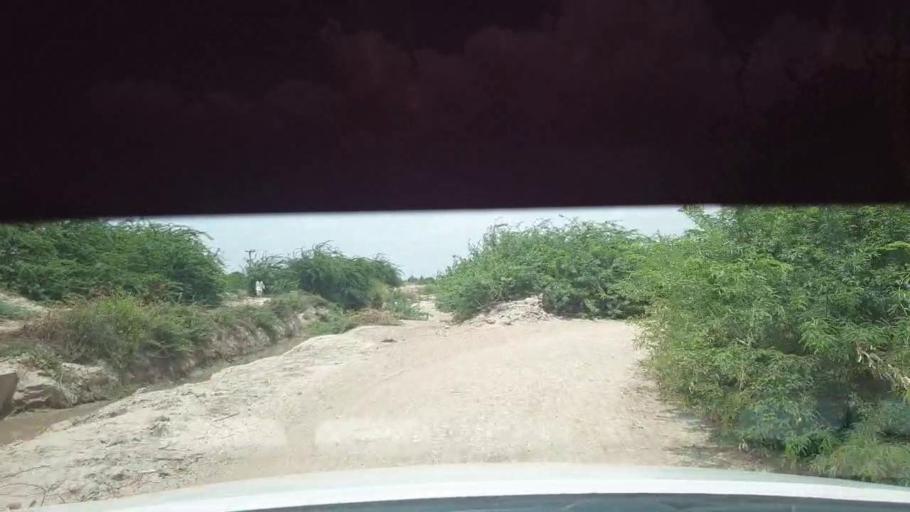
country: PK
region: Sindh
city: Kadhan
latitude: 24.5312
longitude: 69.1281
